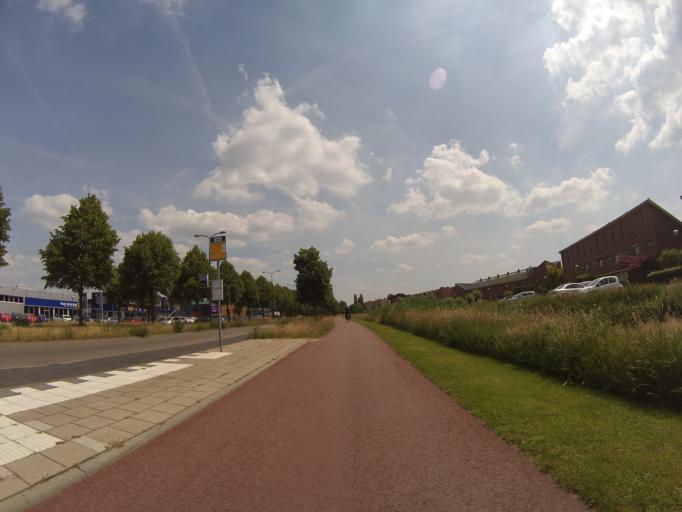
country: NL
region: Utrecht
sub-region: Gemeente Soest
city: Soest
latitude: 52.1763
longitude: 5.2732
